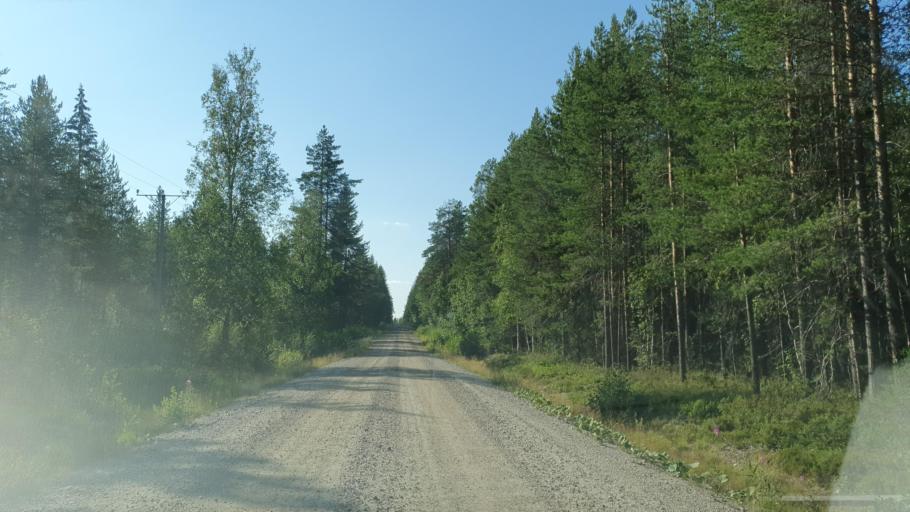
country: FI
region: Kainuu
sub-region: Kehys-Kainuu
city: Kuhmo
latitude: 64.0229
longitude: 29.7283
